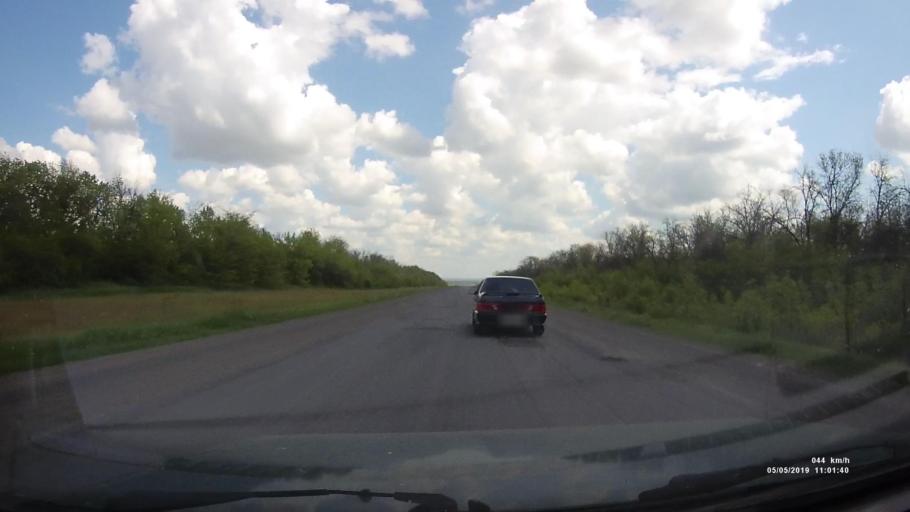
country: RU
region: Rostov
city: Ust'-Donetskiy
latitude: 47.6805
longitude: 40.9009
